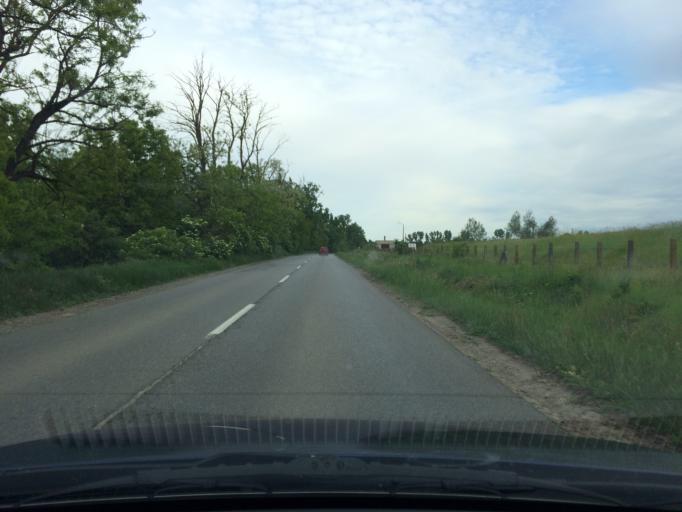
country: HU
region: Szabolcs-Szatmar-Bereg
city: Tiszavasvari
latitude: 47.9370
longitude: 21.3820
